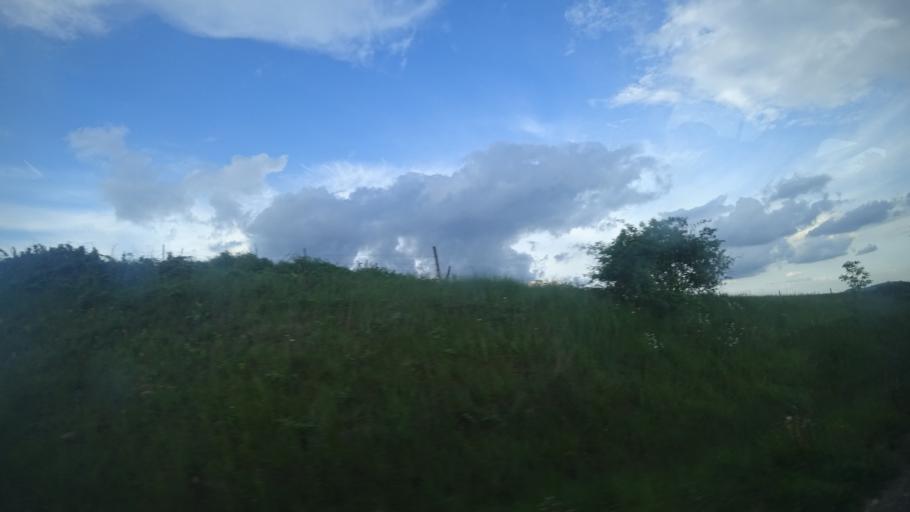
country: FR
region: Midi-Pyrenees
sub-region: Departement de l'Aveyron
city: Millau
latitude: 44.2036
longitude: 3.0144
